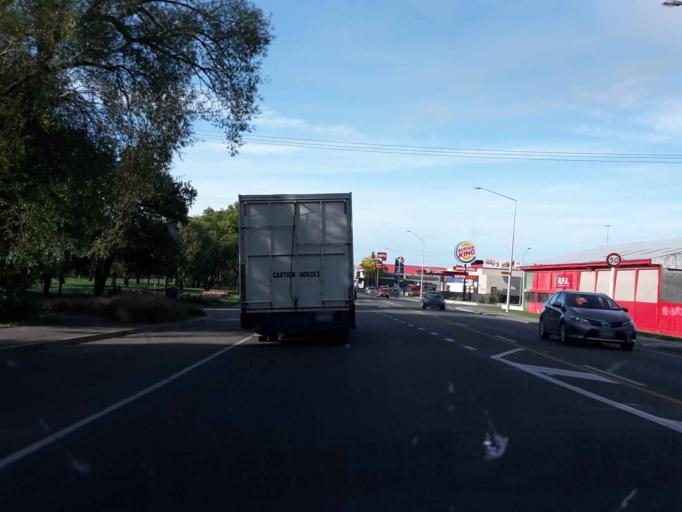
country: NZ
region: Canterbury
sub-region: Ashburton District
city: Ashburton
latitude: -43.9088
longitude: 171.7409
